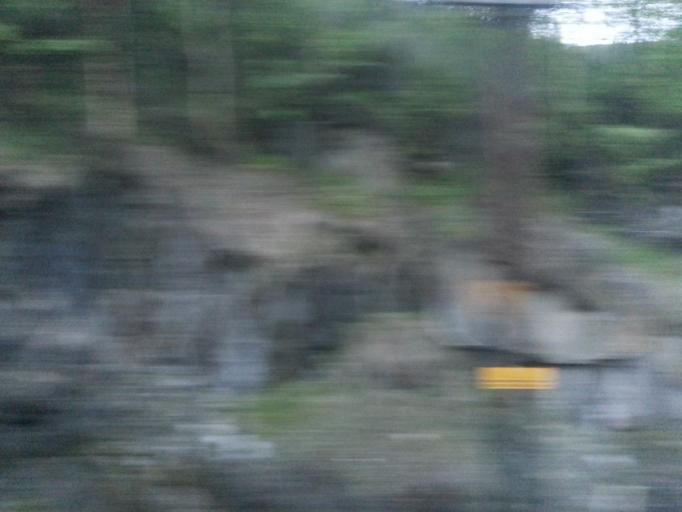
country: NO
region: Oppland
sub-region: Dovre
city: Dombas
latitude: 62.0705
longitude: 9.1268
